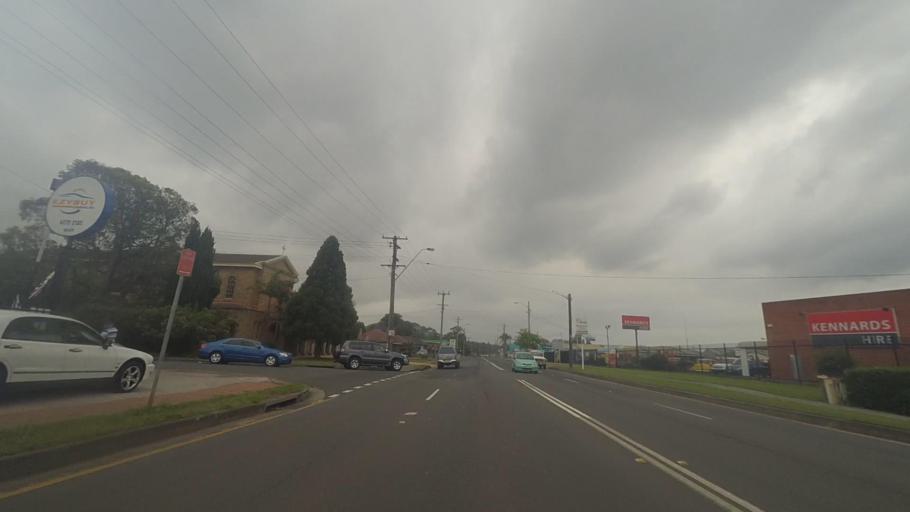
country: AU
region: New South Wales
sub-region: Wollongong
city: Cordeaux Heights
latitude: -34.4531
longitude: 150.8464
